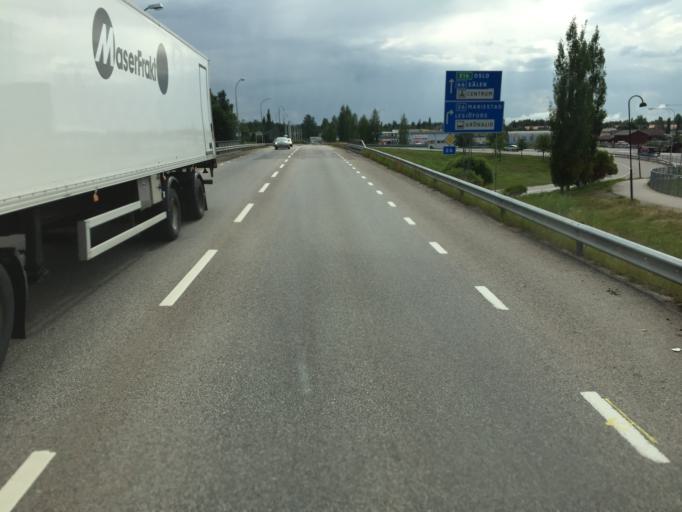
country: SE
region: Dalarna
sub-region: Vansbro Kommun
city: Vansbro
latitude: 60.5117
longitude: 14.2380
